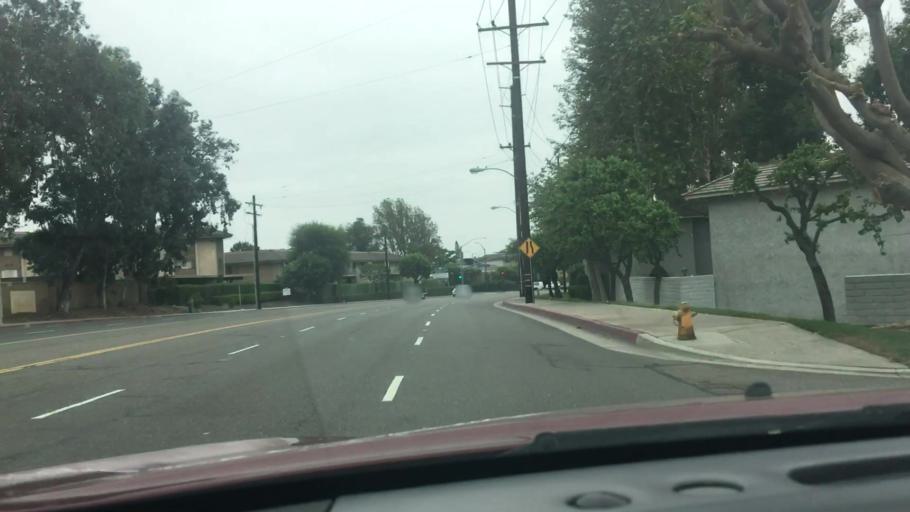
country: US
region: California
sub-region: Orange County
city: Buena Park
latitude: 33.8830
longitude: -117.9938
